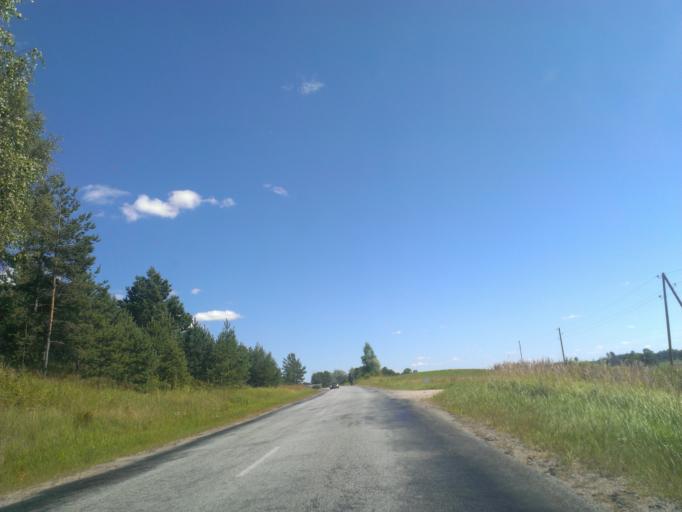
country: LV
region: Sigulda
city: Sigulda
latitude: 57.0233
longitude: 24.8288
